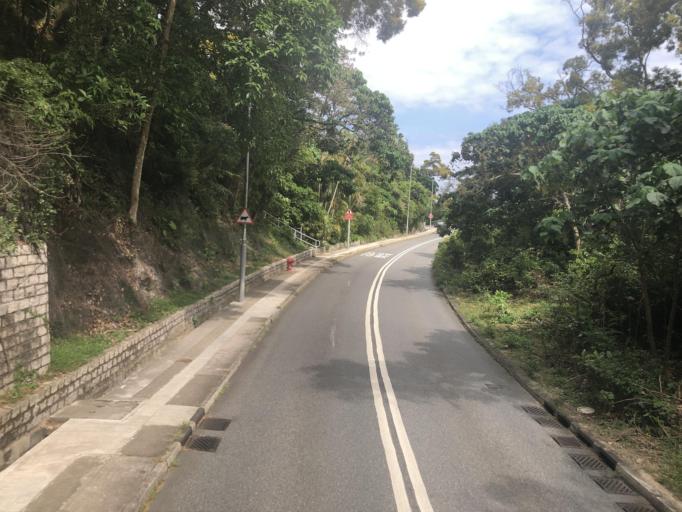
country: HK
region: Sai Kung
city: Sai Kung
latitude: 22.3894
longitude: 114.2919
